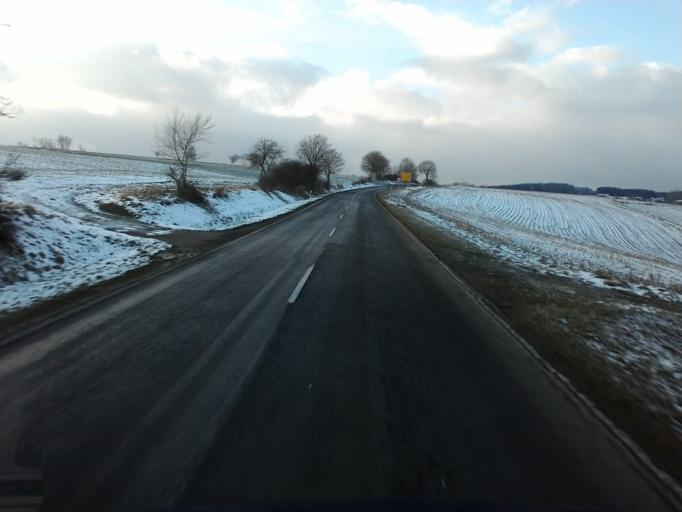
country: DE
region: Rheinland-Pfalz
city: Habscheid
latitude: 50.1926
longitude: 6.2478
